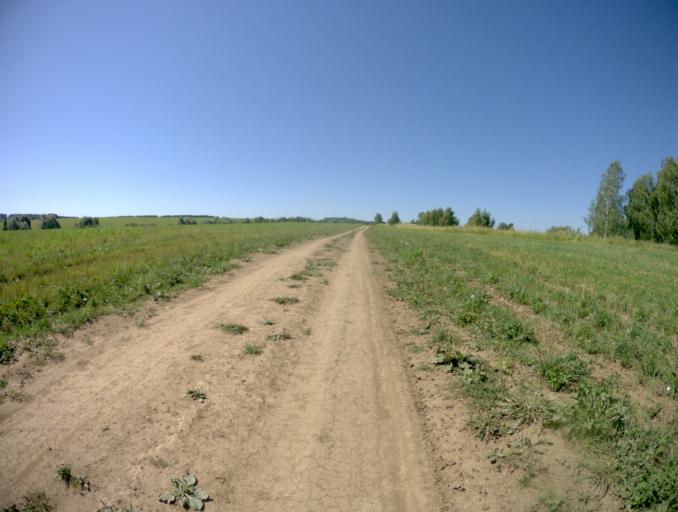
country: RU
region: Nizjnij Novgorod
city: Reshetikha
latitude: 56.1550
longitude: 43.3292
